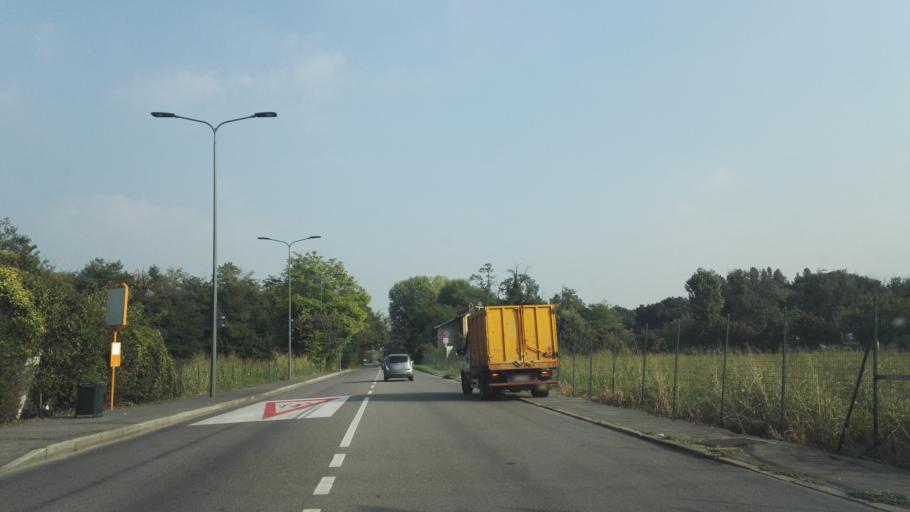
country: IT
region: Lombardy
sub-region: Citta metropolitana di Milano
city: Figino
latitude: 45.4893
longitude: 9.0726
